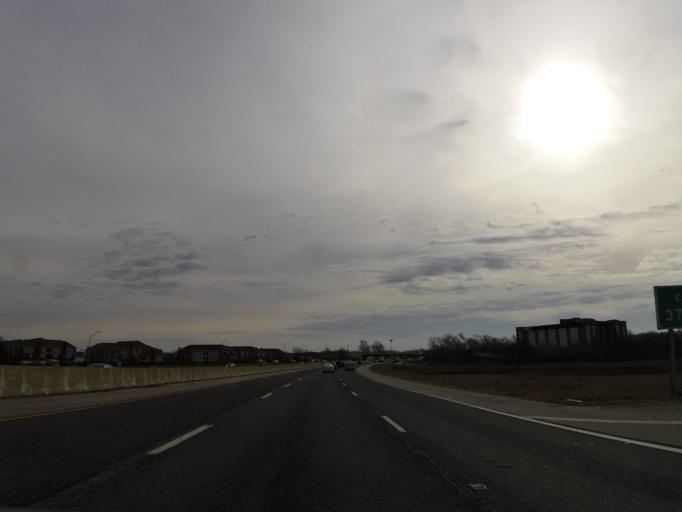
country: US
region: Indiana
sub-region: Marion County
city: Lawrence
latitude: 39.8944
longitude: -86.0534
